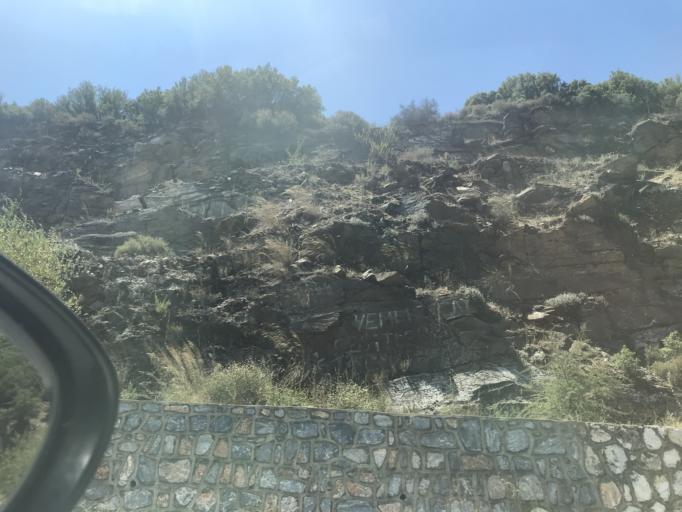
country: TR
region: Aydin
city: Akcaova
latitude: 37.5028
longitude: 28.1041
